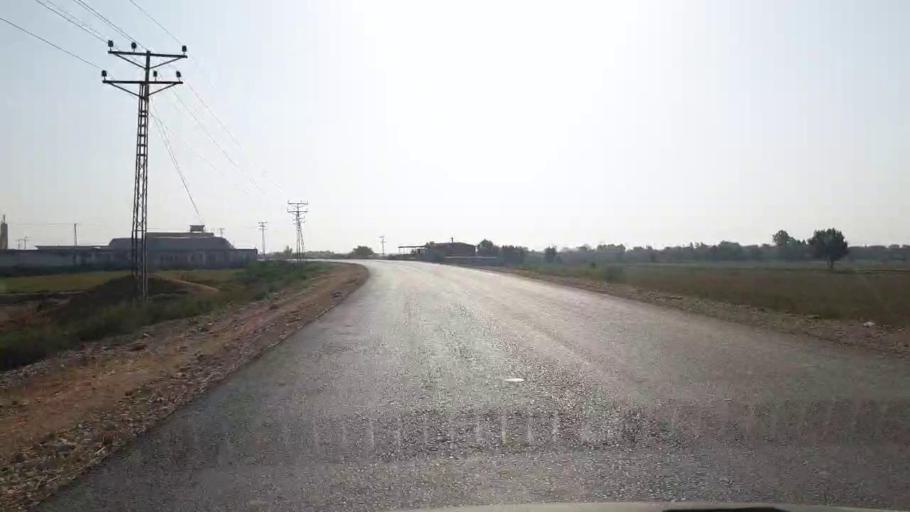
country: PK
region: Sindh
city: Badin
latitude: 24.6609
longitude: 68.8787
